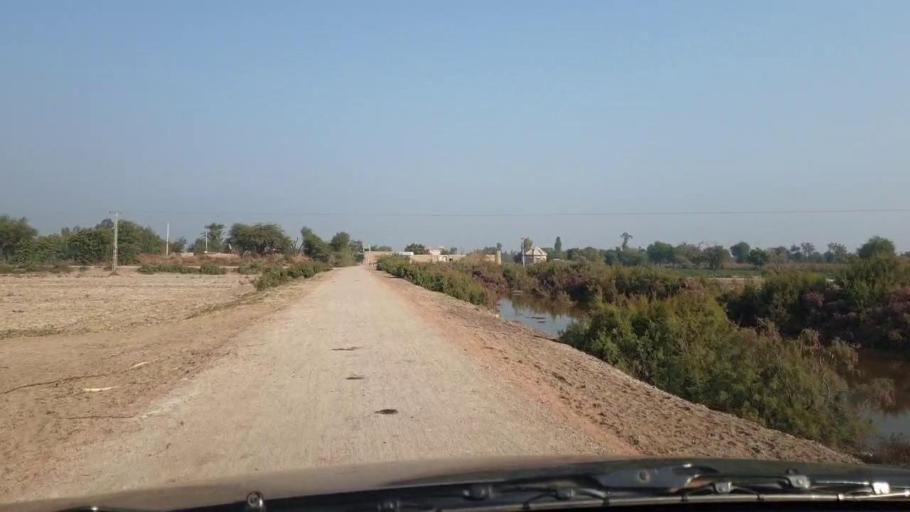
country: PK
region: Sindh
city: Sanghar
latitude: 25.9840
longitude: 68.9519
